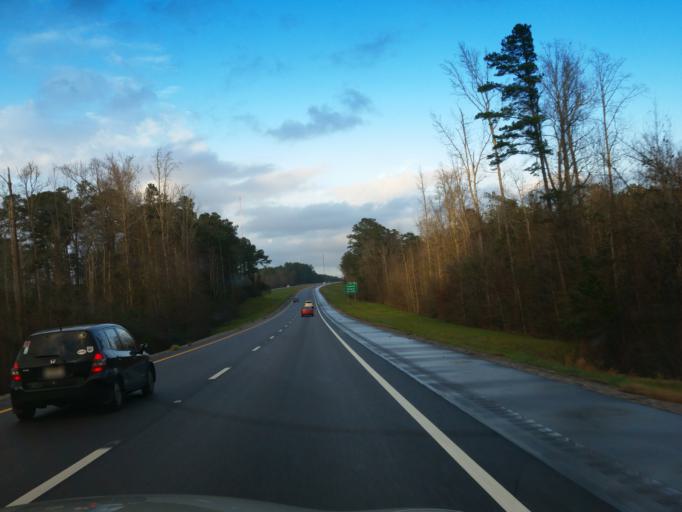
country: US
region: Mississippi
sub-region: Jones County
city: Sharon
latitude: 31.9556
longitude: -88.9762
